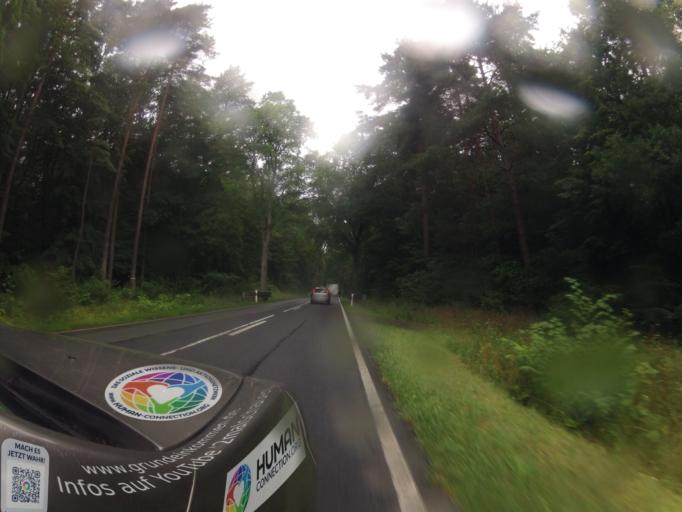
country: DE
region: Mecklenburg-Vorpommern
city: Usedom
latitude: 53.9069
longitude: 14.0290
